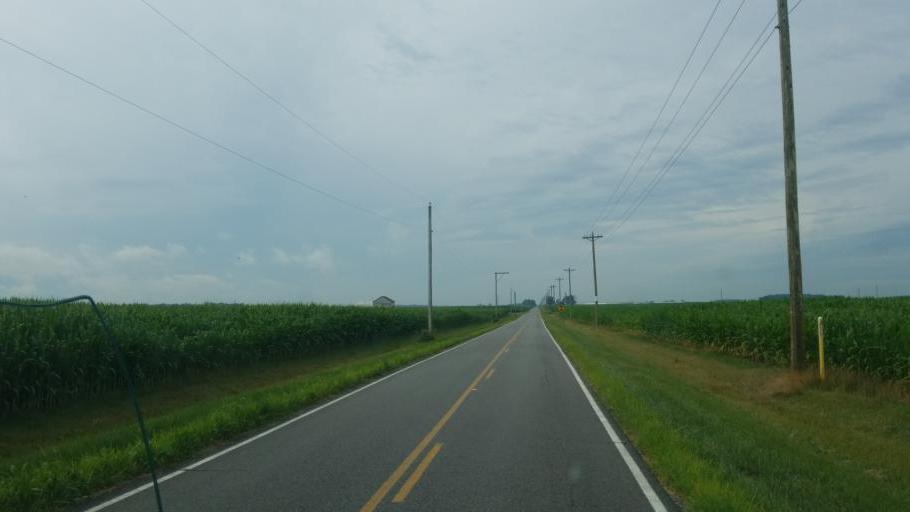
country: US
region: Ohio
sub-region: Defiance County
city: Hicksville
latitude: 41.3282
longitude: -84.6900
